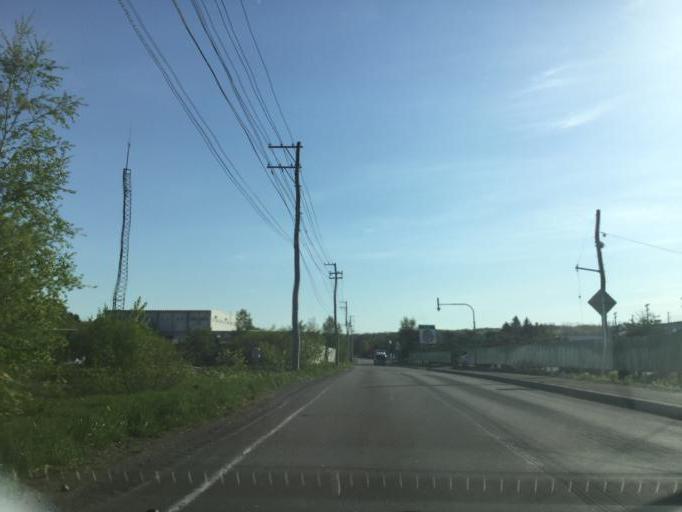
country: JP
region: Hokkaido
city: Kitahiroshima
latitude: 43.0066
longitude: 141.5539
